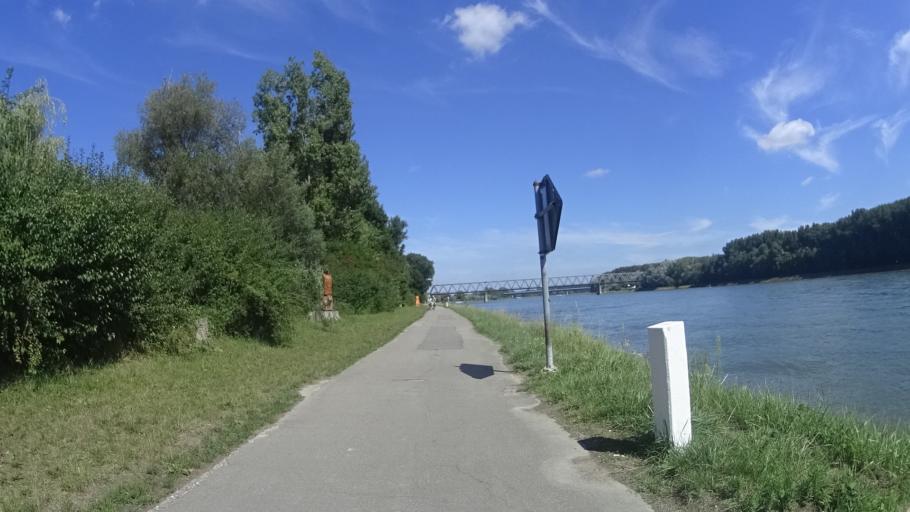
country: DE
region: Rheinland-Pfalz
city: Germersheim
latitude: 49.2129
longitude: 8.3848
